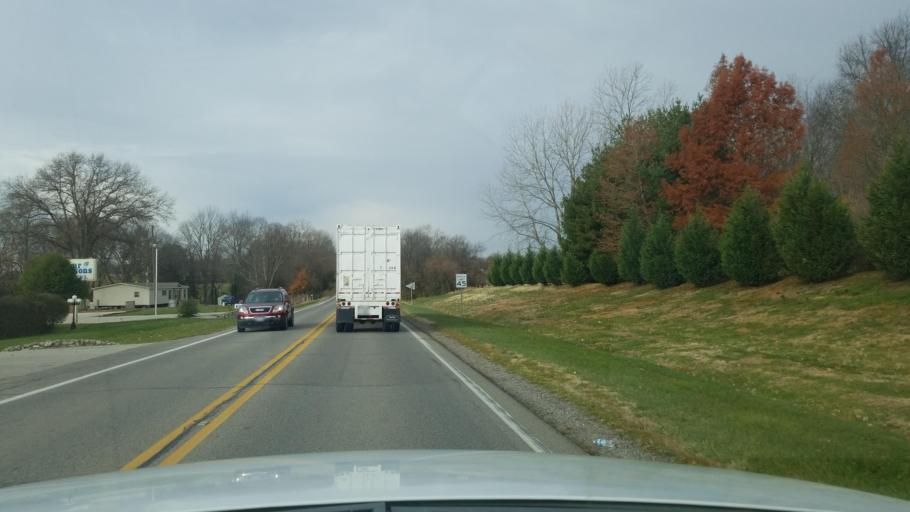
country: US
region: Indiana
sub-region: Posey County
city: Mount Vernon
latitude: 37.9290
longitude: -87.9274
